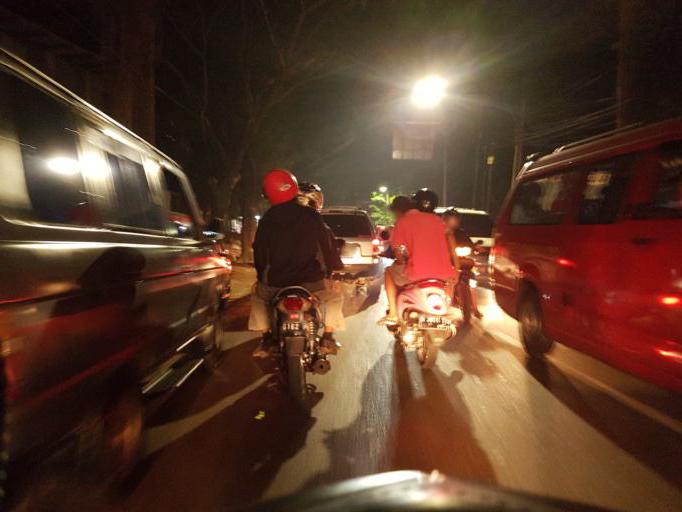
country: ID
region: West Java
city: Cileungsir
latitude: -6.3141
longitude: 106.9114
